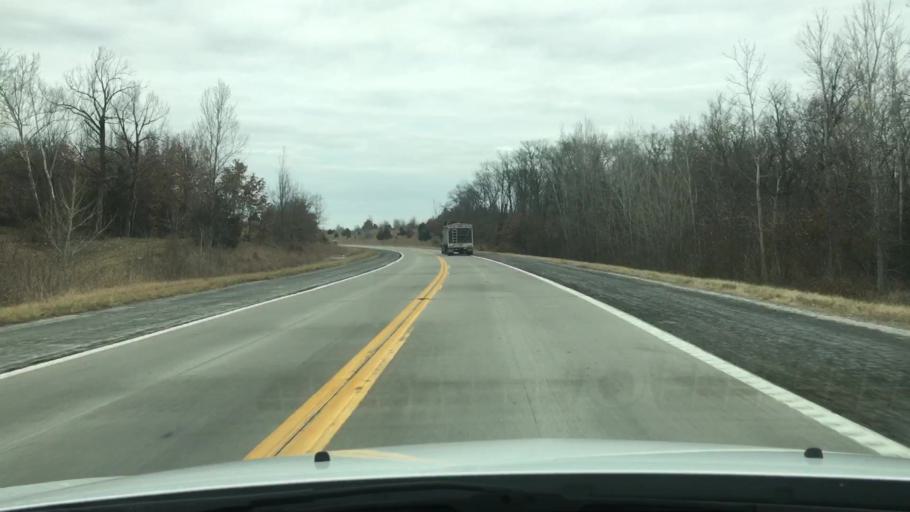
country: US
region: Missouri
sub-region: Audrain County
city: Mexico
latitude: 39.1465
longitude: -91.8445
